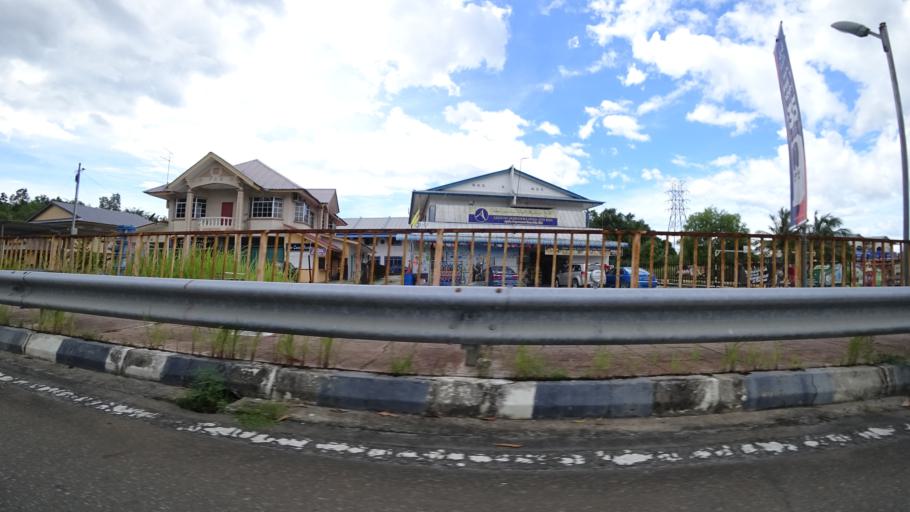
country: BN
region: Brunei and Muara
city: Bandar Seri Begawan
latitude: 4.9703
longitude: 115.0216
